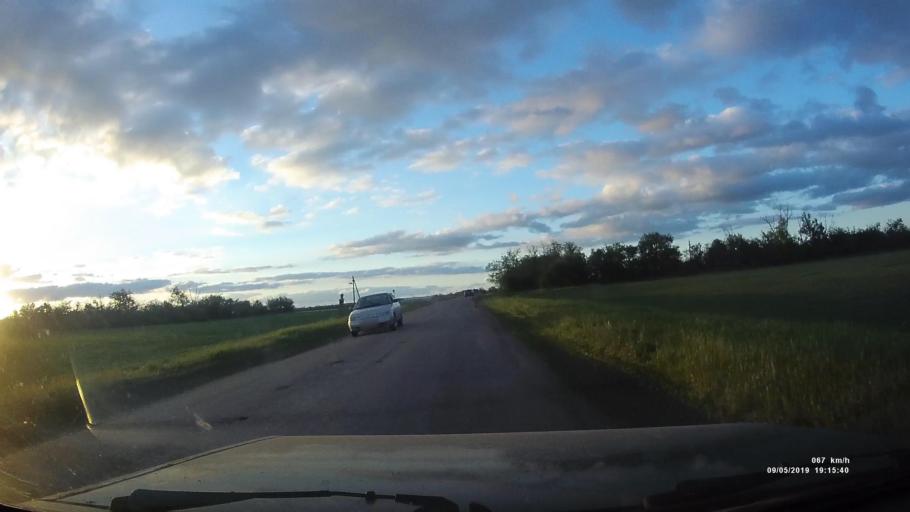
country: RU
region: Krasnodarskiy
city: Kanelovskaya
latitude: 46.7703
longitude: 39.2113
